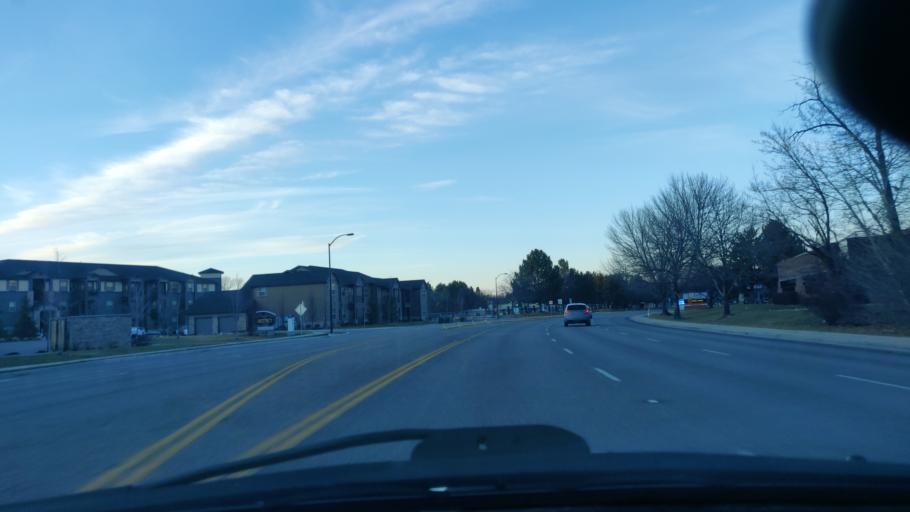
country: US
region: Idaho
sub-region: Ada County
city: Boise
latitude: 43.5922
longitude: -116.1775
